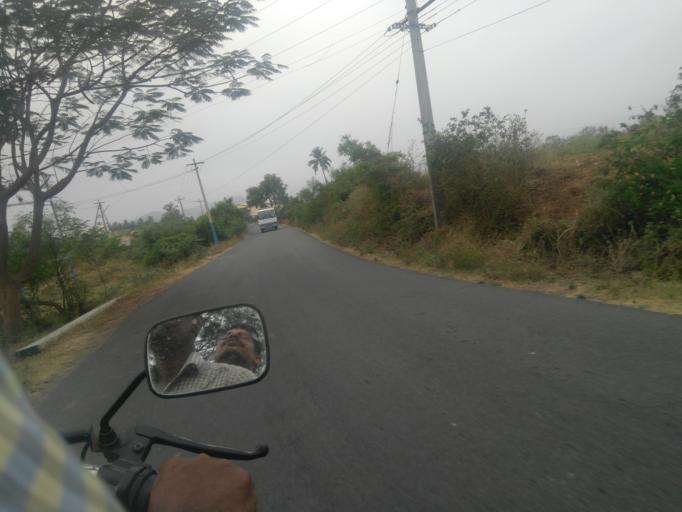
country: IN
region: Tamil Nadu
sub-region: Coimbatore
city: Karamadai
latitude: 11.2606
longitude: 76.9455
